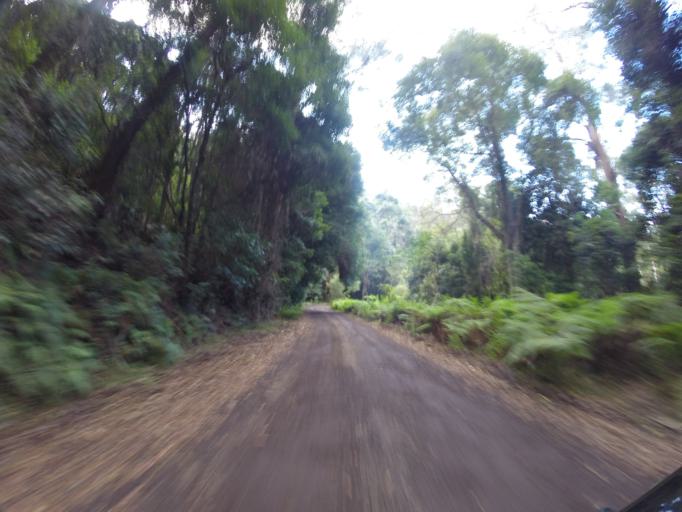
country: AU
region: New South Wales
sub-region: Wollongong
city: Cordeaux Heights
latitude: -34.4367
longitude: 150.7906
